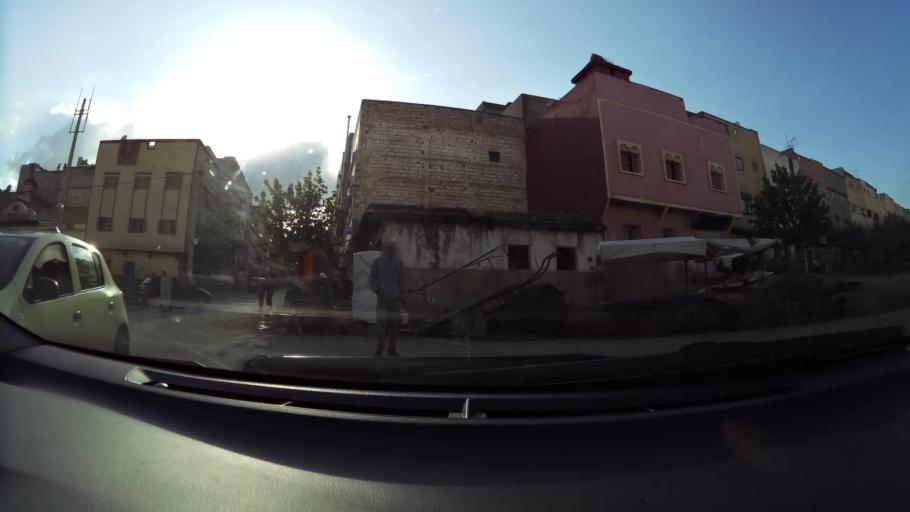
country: MA
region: Chaouia-Ouardigha
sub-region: Settat Province
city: Settat
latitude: 33.0048
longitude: -7.6279
